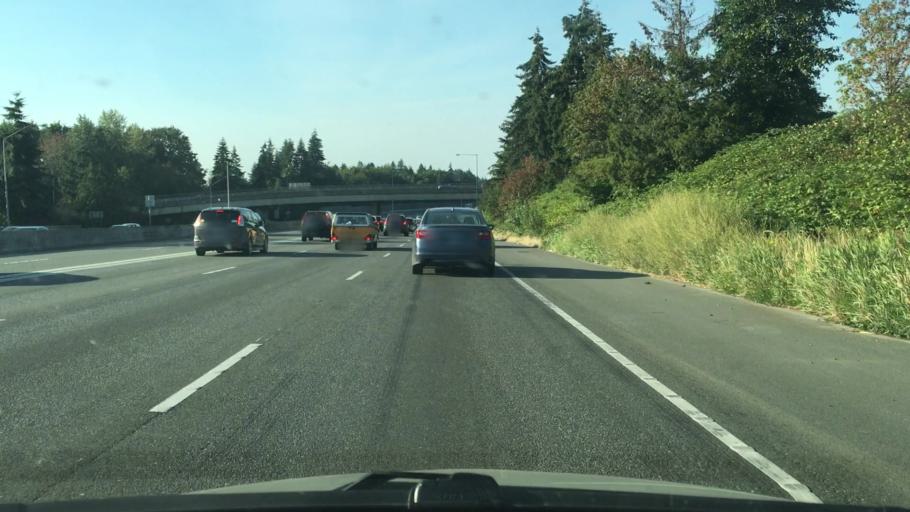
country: US
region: Washington
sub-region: King County
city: Kirkland
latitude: 47.6677
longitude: -122.1868
